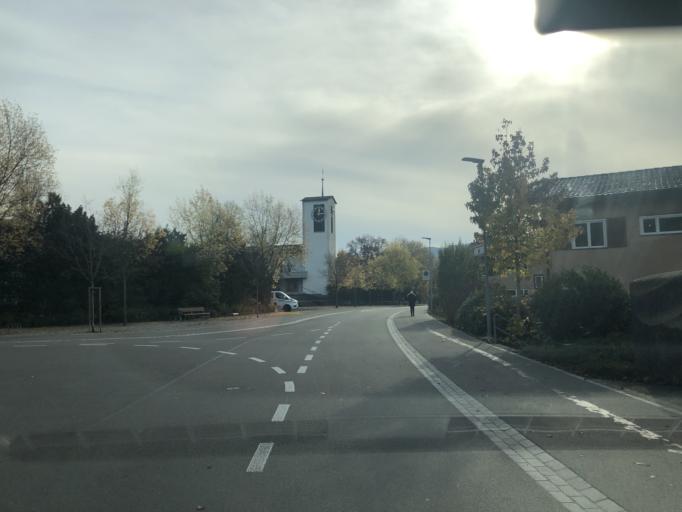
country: CH
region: Aargau
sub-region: Bezirk Baden
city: Wettingen
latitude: 47.4640
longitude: 8.3180
